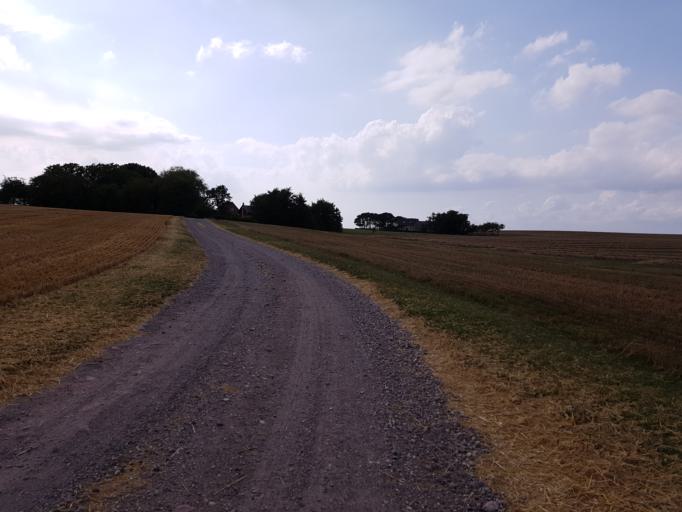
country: DK
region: Zealand
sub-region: Guldborgsund Kommune
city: Nykobing Falster
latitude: 54.6004
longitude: 11.9245
